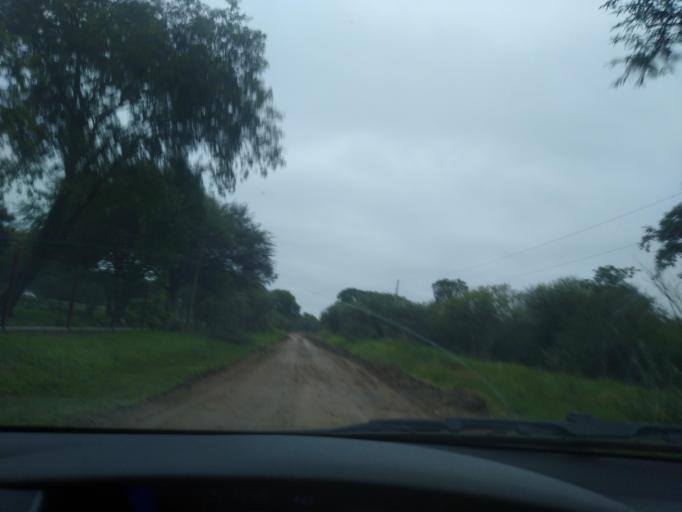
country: AR
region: Chaco
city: Colonia Benitez
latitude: -27.3304
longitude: -58.9642
